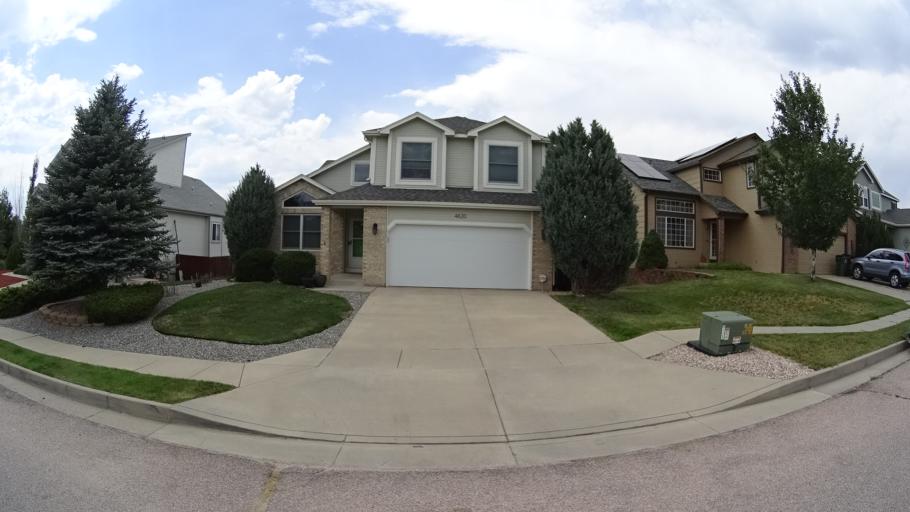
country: US
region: Colorado
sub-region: El Paso County
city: Black Forest
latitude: 38.9608
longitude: -104.7408
